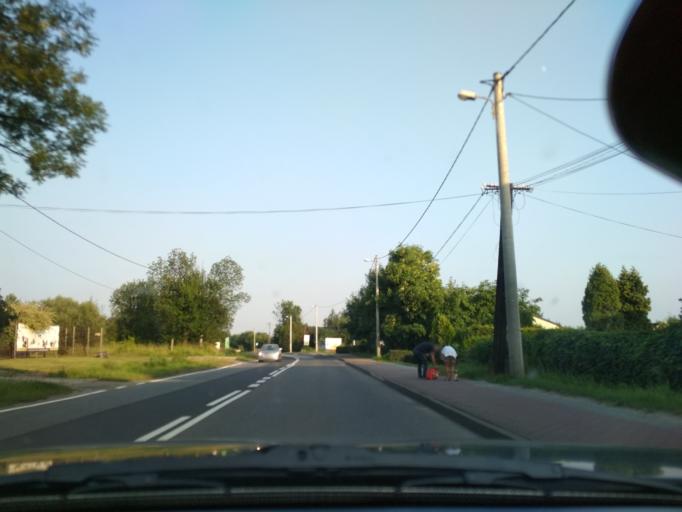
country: PL
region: Silesian Voivodeship
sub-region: Powiat zawiercianski
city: Ogrodzieniec
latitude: 50.4574
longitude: 19.5009
